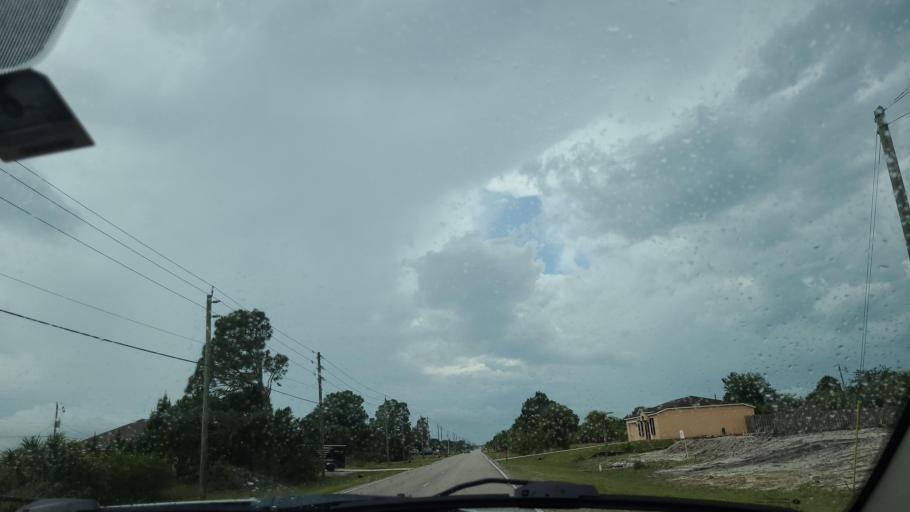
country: US
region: Florida
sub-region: Brevard County
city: Grant-Valkaria
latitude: 27.9529
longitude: -80.6842
